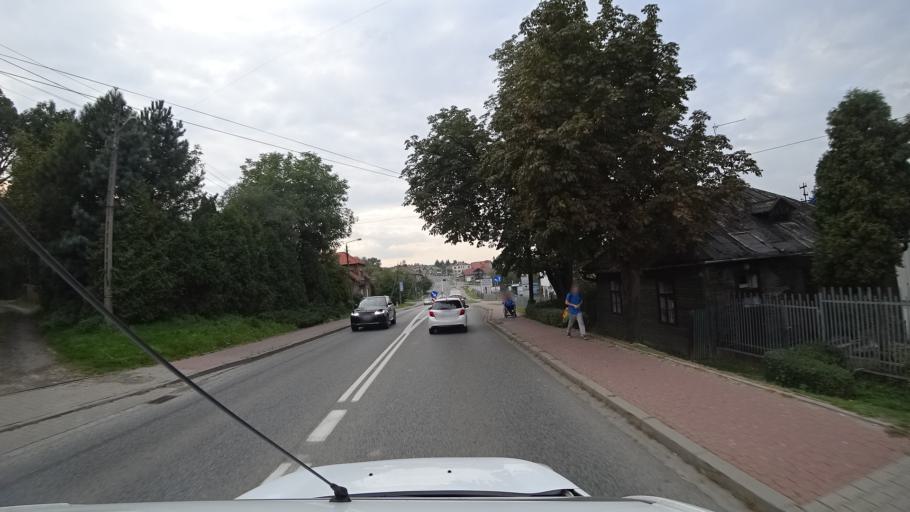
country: PL
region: Lesser Poland Voivodeship
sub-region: Powiat wadowicki
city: Kalwaria Zebrzydowska
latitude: 49.8707
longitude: 19.6695
